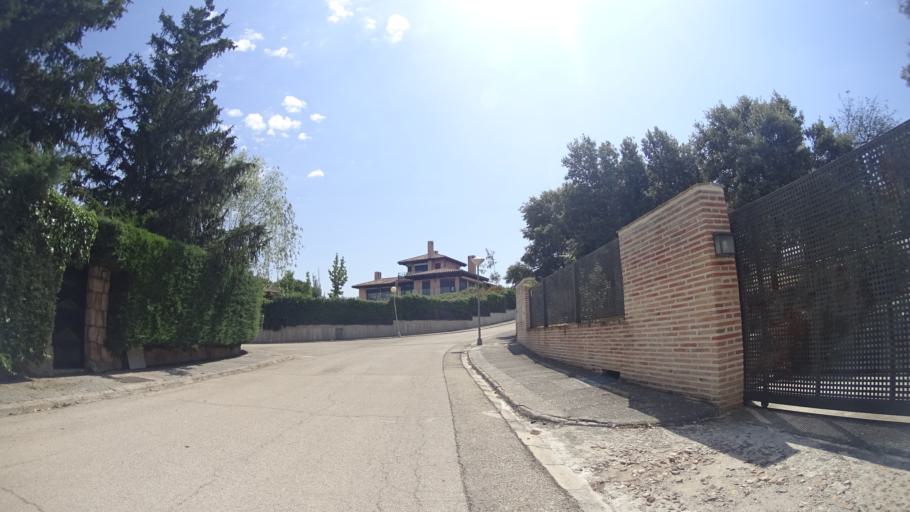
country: ES
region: Madrid
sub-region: Provincia de Madrid
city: Torrelodones
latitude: 40.5998
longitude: -3.9363
